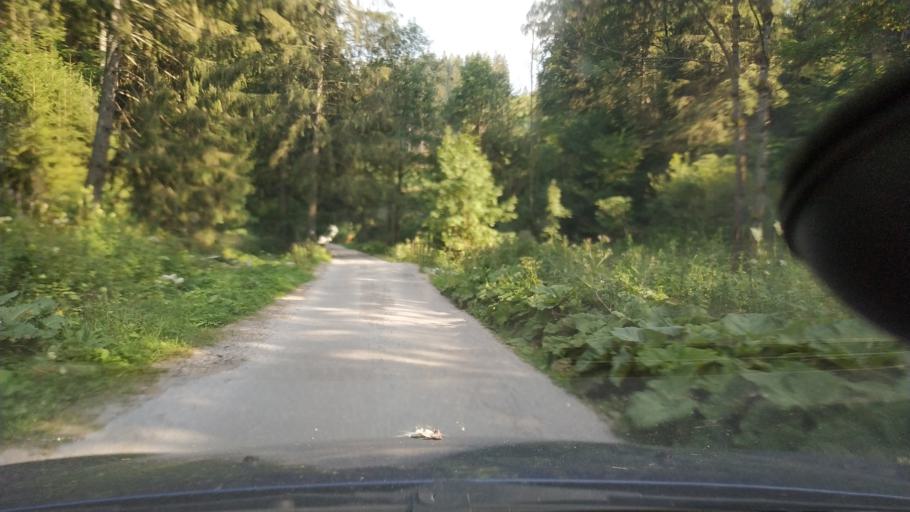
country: SK
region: Zilinsky
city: Ruzomberok
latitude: 48.9964
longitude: 19.2623
